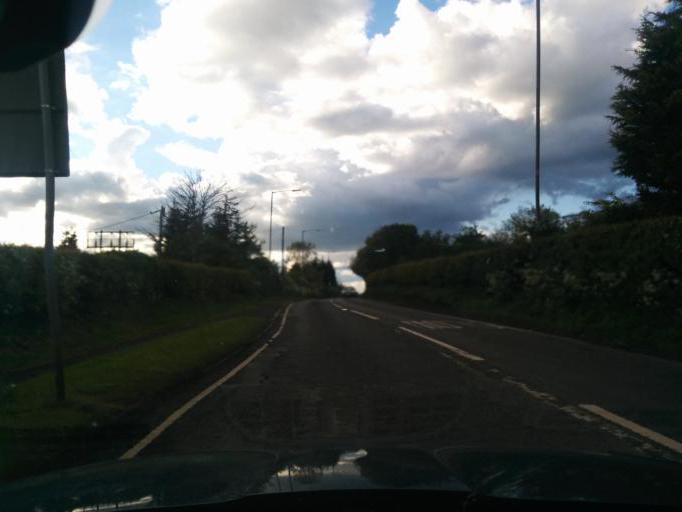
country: GB
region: England
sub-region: Northumberland
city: Bedlington
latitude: 55.1401
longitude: -1.5986
